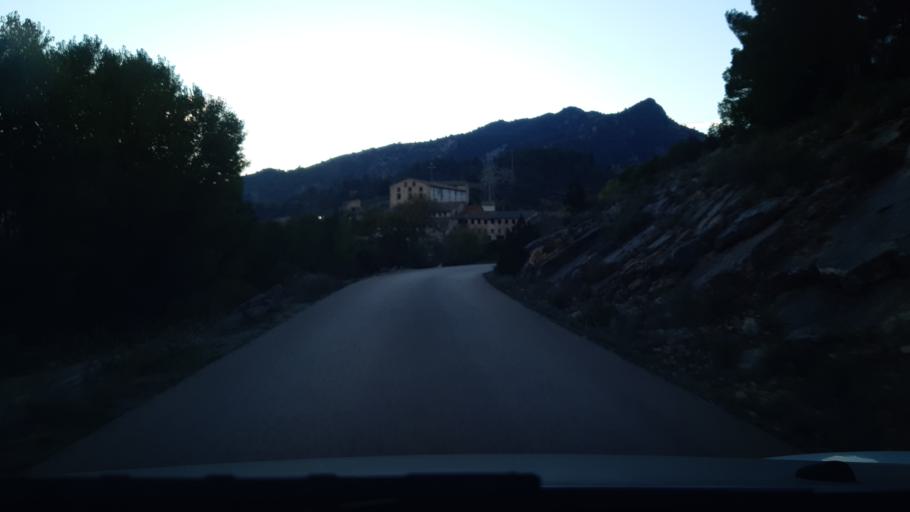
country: ES
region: Aragon
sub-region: Provincia de Teruel
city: Valderrobres
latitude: 40.8392
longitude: 0.1886
